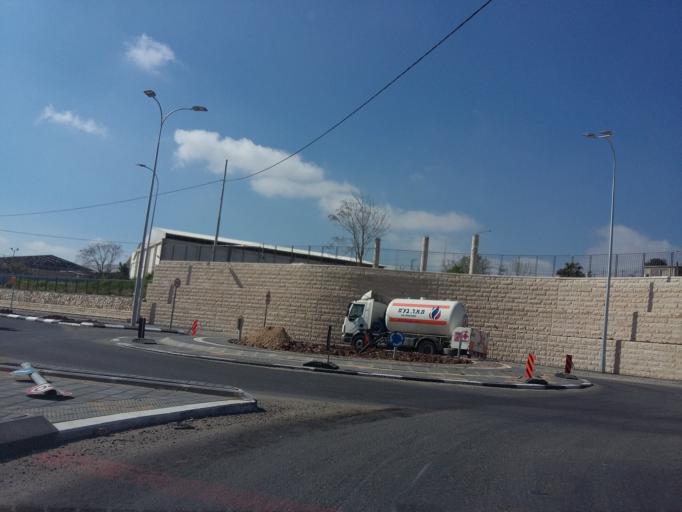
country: PS
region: West Bank
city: Ar Ram wa Dahiyat al Barid
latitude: 31.8531
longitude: 35.2246
